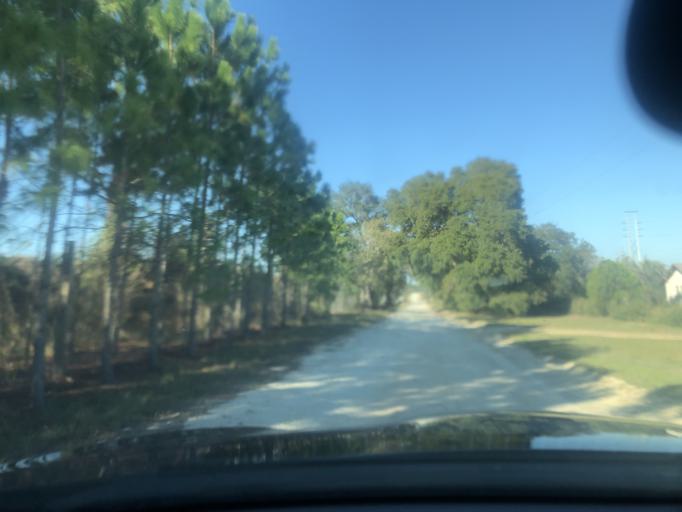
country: US
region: Florida
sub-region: Citrus County
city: Lecanto
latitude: 28.8189
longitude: -82.5180
